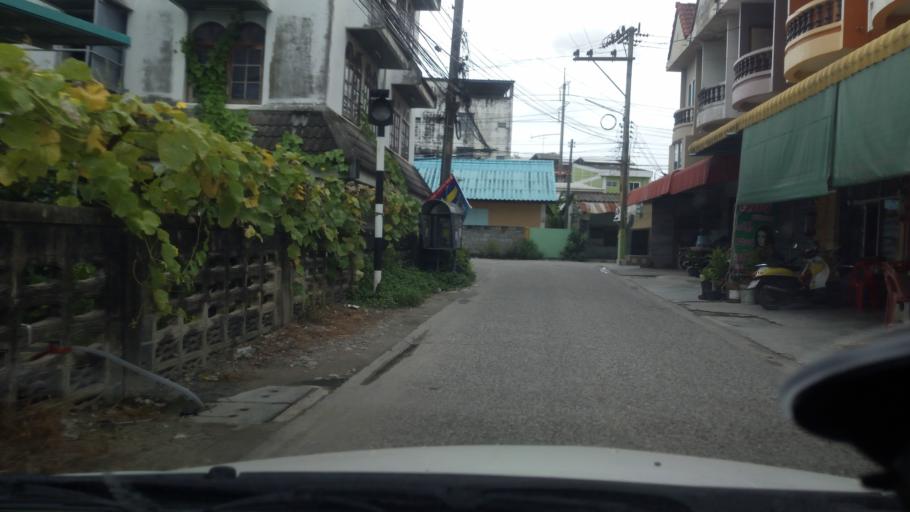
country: TH
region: Chon Buri
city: Phan Thong
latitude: 13.4134
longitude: 101.0584
